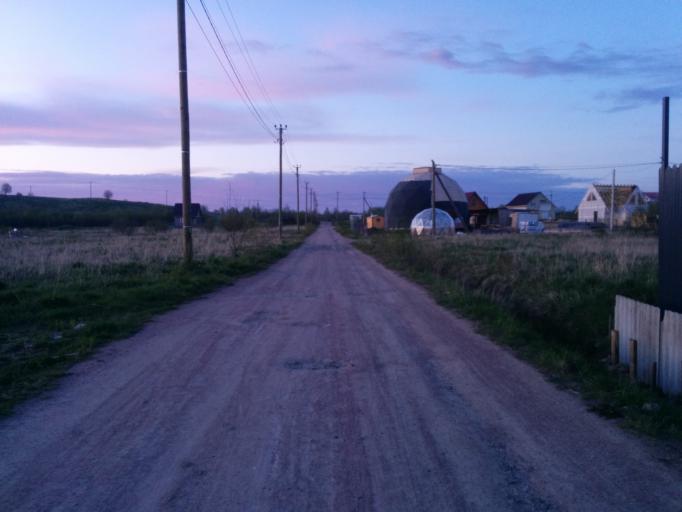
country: RU
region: Leningrad
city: Verkhniye Osel'ki
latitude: 60.2654
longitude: 30.4227
